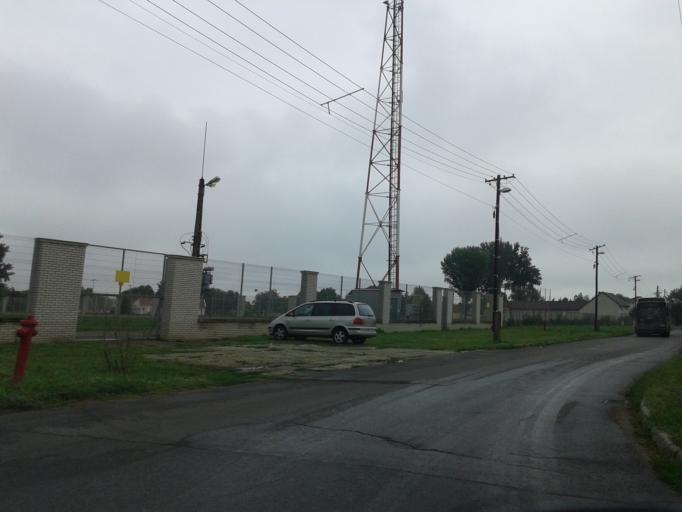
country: HU
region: Csongrad
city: Szeged
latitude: 46.2462
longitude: 20.1223
